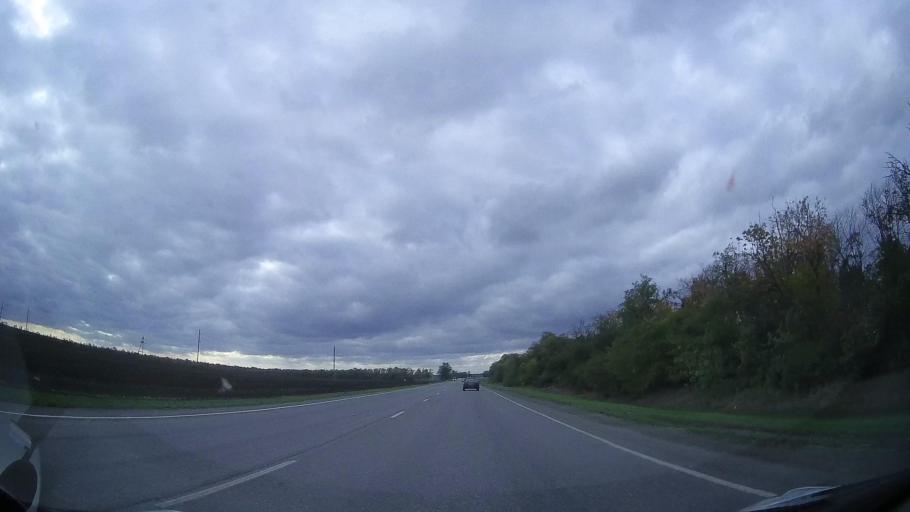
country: RU
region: Rostov
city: Zernograd
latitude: 46.8151
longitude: 40.2760
